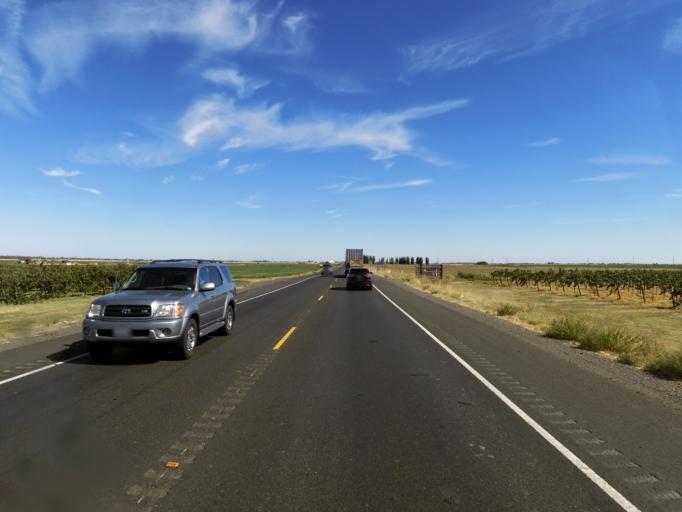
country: US
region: California
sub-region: Solano County
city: Rio Vista
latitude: 38.1528
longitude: -121.6703
